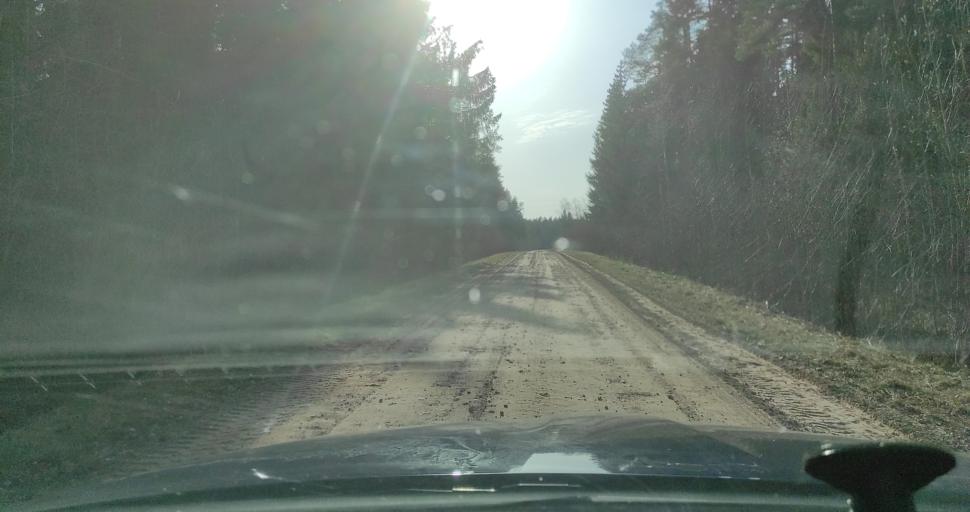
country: LV
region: Kuldigas Rajons
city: Kuldiga
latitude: 57.0000
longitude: 22.0185
